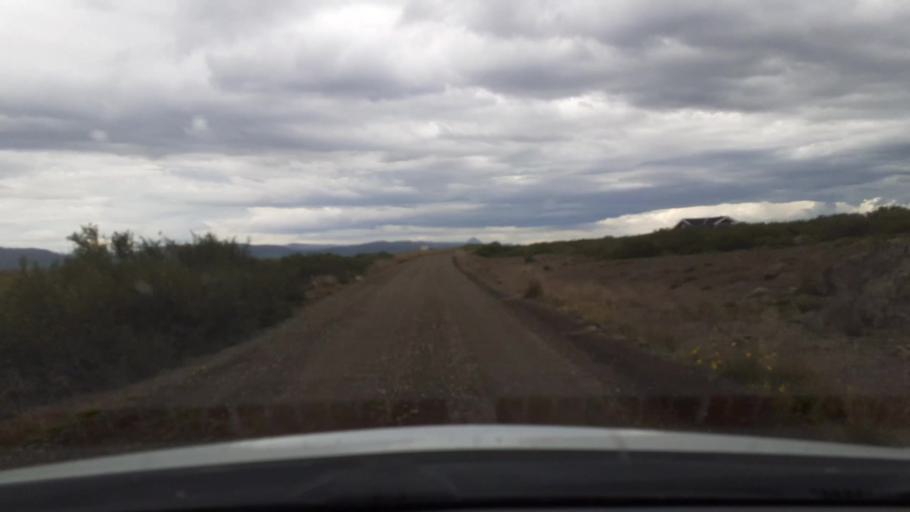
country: IS
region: West
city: Borgarnes
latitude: 64.6456
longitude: -21.8929
